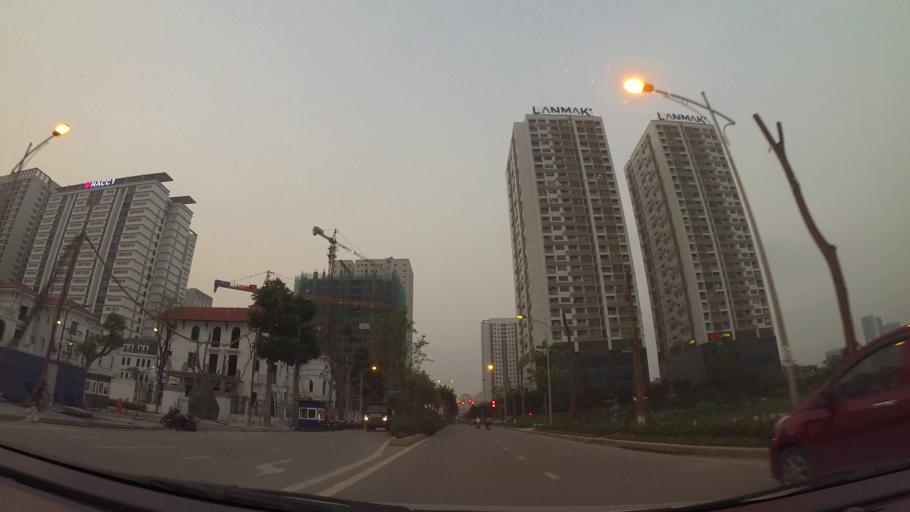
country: VN
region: Ha Noi
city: Tay Ho
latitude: 21.0633
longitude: 105.8008
